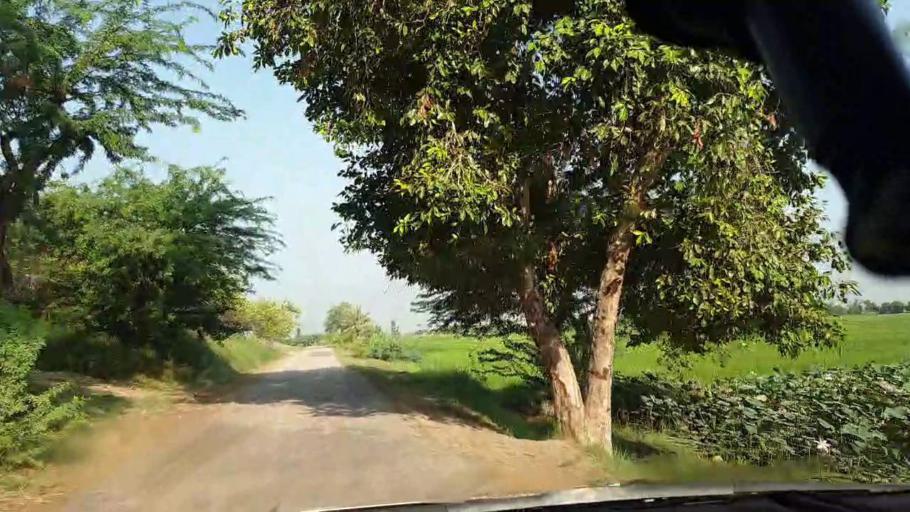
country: PK
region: Sindh
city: Larkana
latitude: 27.6202
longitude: 68.2109
